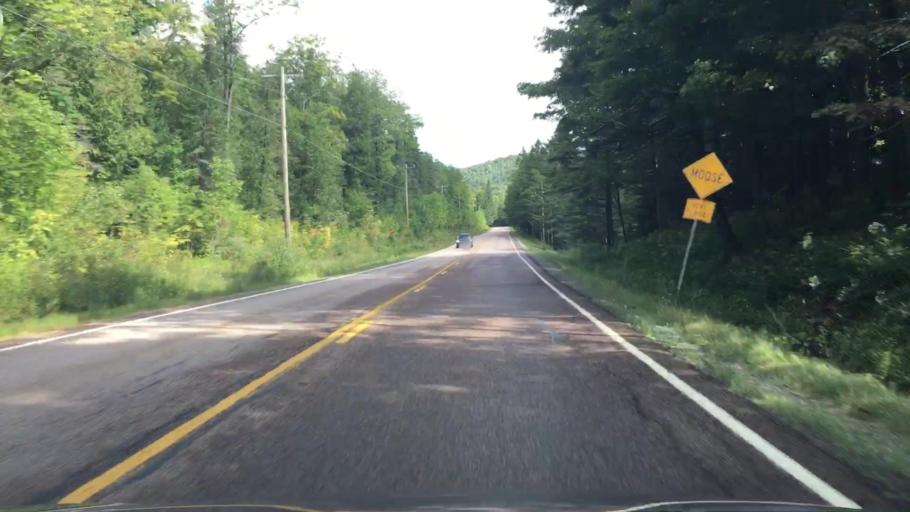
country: US
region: Vermont
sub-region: Washington County
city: South Barre
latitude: 44.1442
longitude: -72.3672
